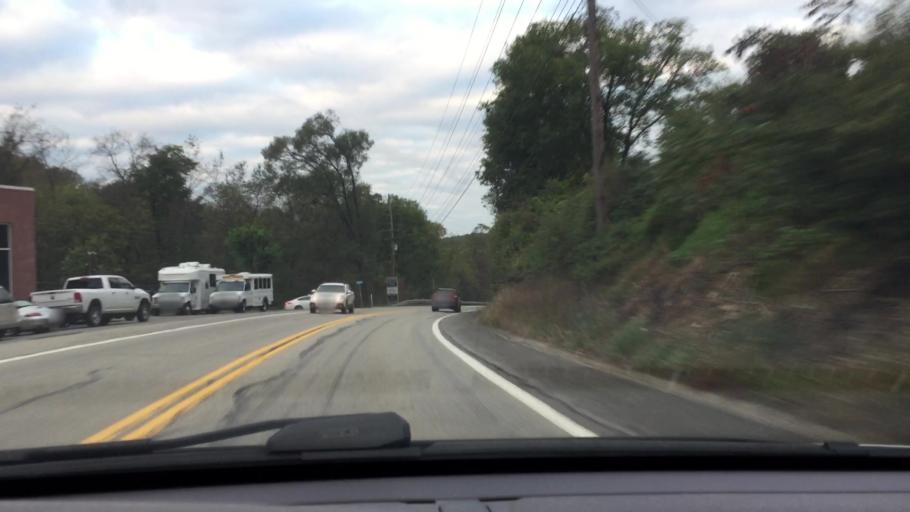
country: US
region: Pennsylvania
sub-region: Washington County
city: Canonsburg
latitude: 40.2421
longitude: -80.1862
